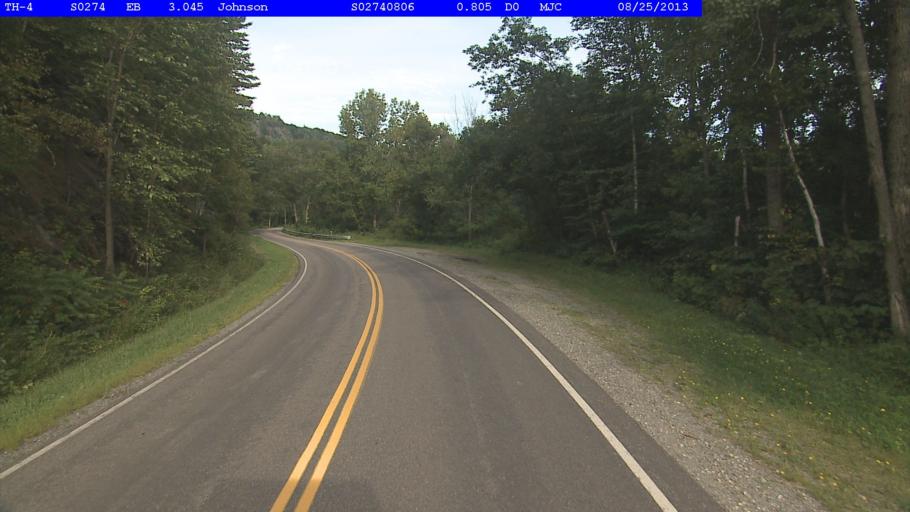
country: US
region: Vermont
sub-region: Lamoille County
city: Johnson
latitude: 44.6525
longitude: -72.7360
